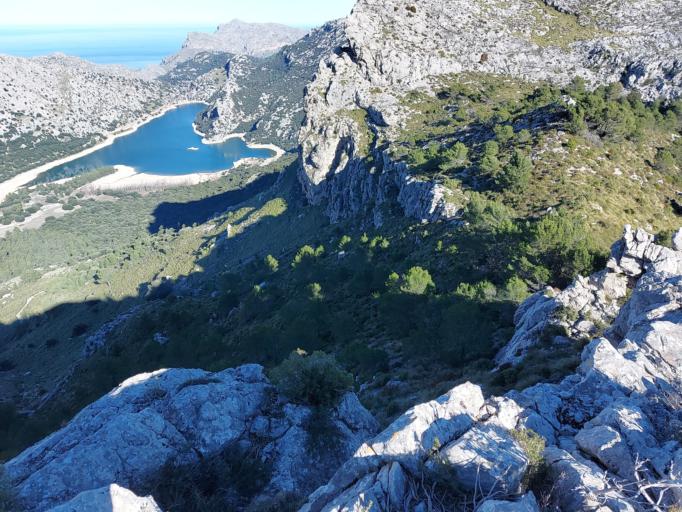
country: ES
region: Balearic Islands
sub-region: Illes Balears
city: Escorca
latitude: 39.7871
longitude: 2.8123
